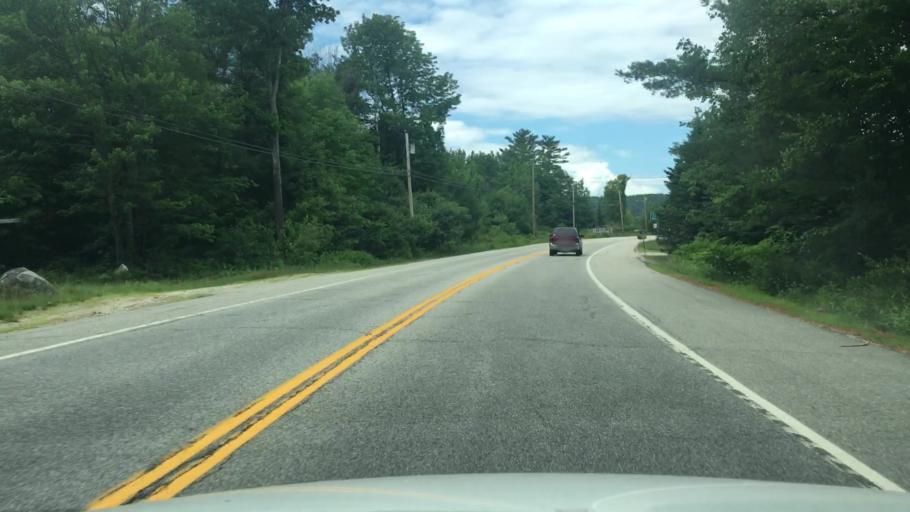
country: US
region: Maine
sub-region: Oxford County
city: West Paris
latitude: 44.3437
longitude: -70.5623
